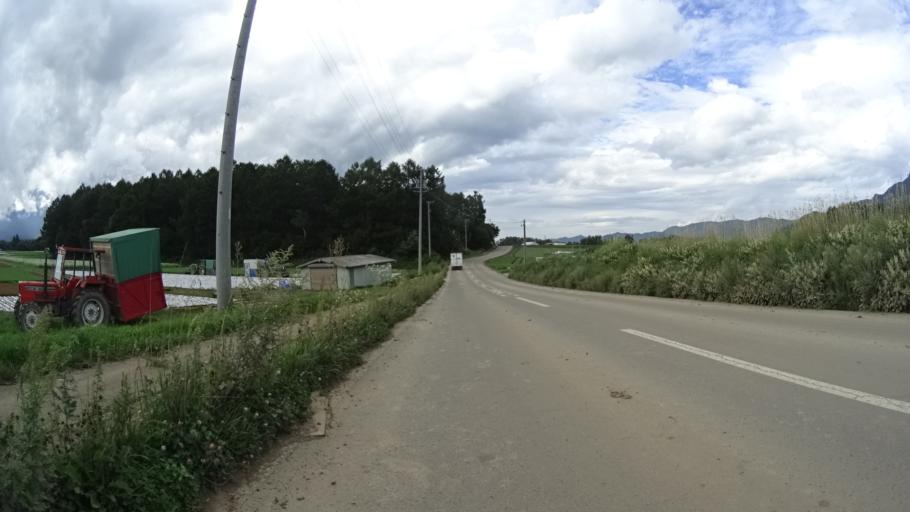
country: JP
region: Nagano
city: Saku
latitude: 35.9682
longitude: 138.5157
